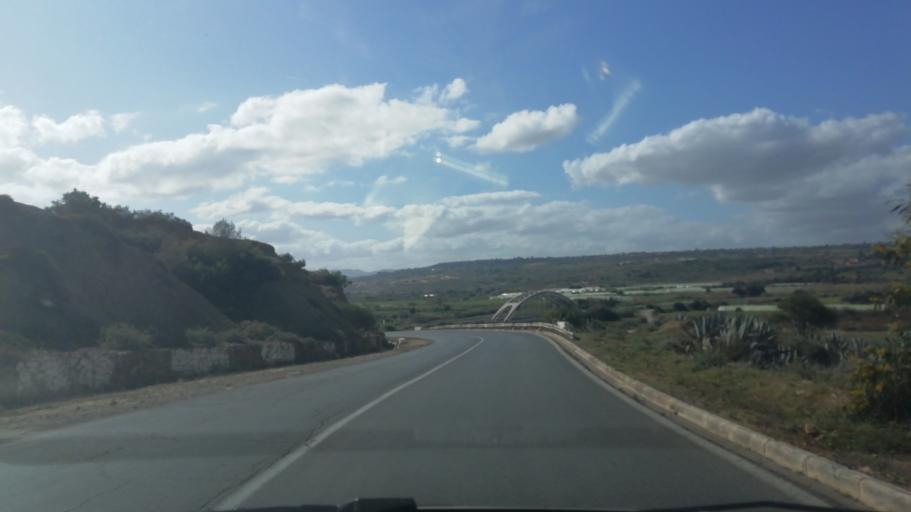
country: DZ
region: Relizane
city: Mazouna
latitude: 36.3068
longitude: 0.6712
